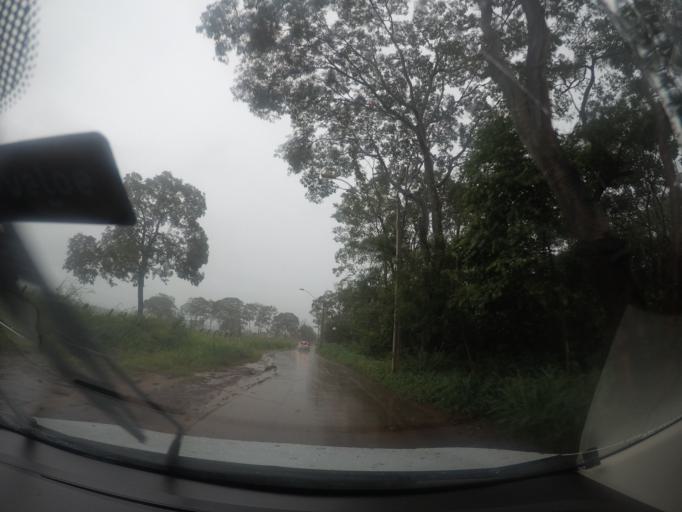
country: BR
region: Goias
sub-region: Goiania
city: Goiania
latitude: -16.5921
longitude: -49.3235
